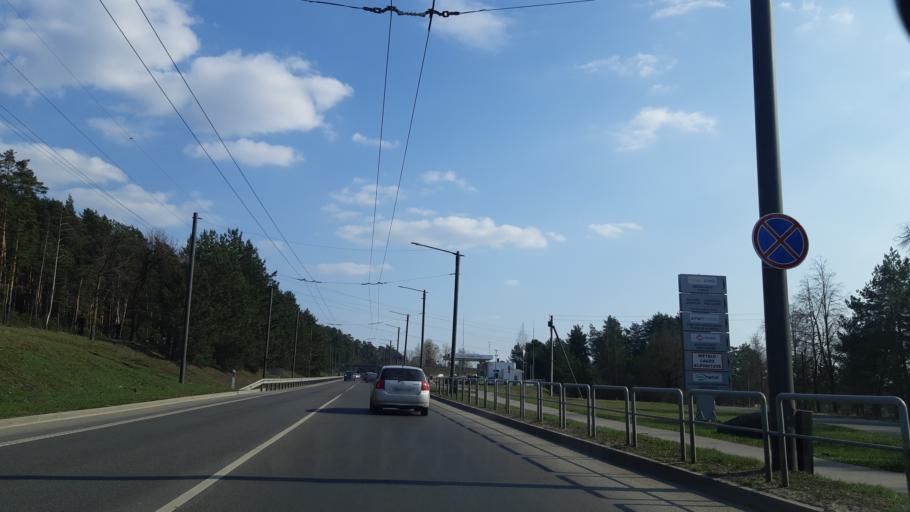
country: LT
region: Kauno apskritis
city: Dainava (Kaunas)
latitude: 54.8821
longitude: 24.0087
